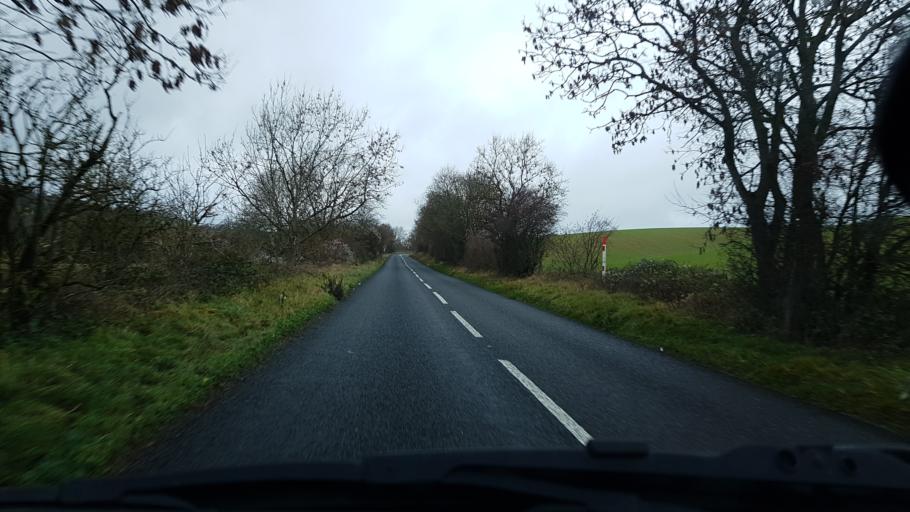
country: GB
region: England
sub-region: Gloucestershire
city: Charlton Kings
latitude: 51.8262
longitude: -2.0417
